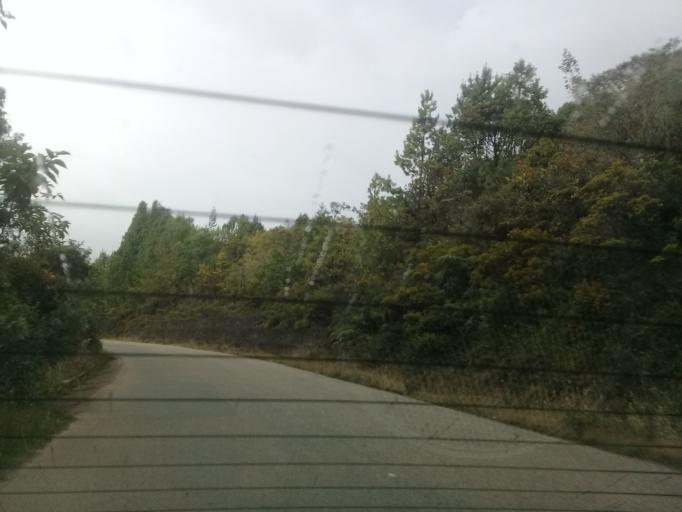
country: CO
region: Cundinamarca
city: Junin
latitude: 4.8458
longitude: -73.7443
